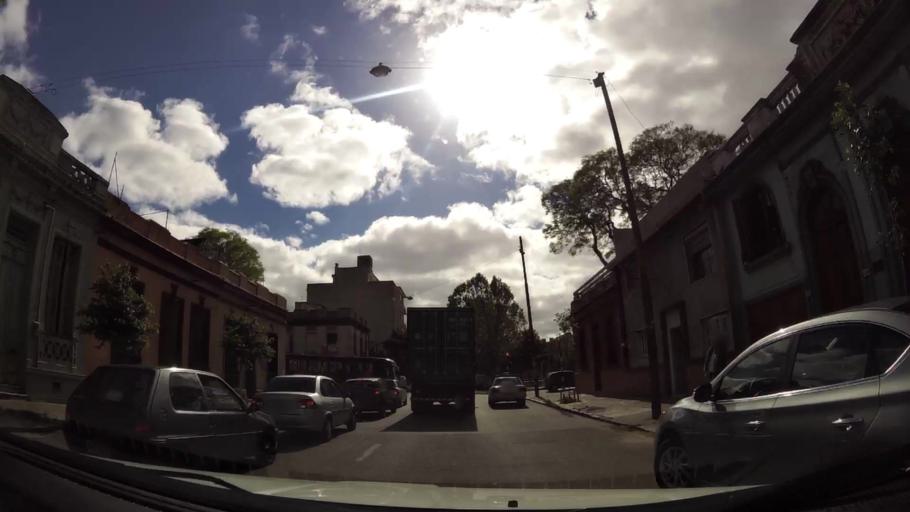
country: UY
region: Montevideo
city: Montevideo
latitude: -34.8963
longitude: -56.1731
